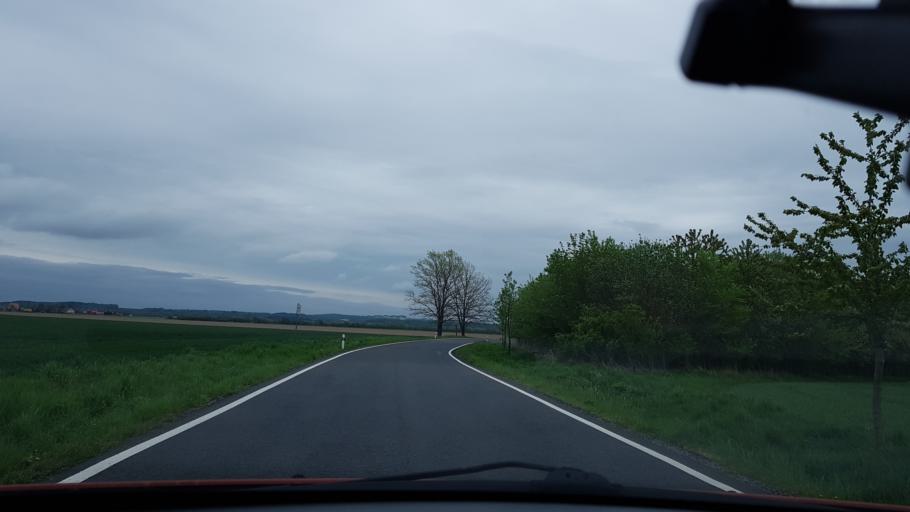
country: CZ
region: Olomoucky
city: Vidnava
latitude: 50.3815
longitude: 17.1514
